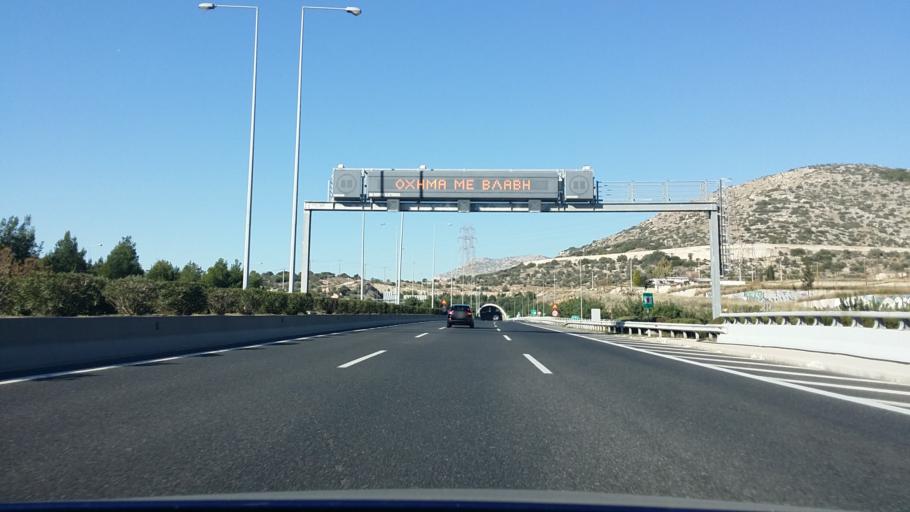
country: GR
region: Attica
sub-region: Nomarchia Dytikis Attikis
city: Ano Liosia
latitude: 38.0790
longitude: 23.6772
